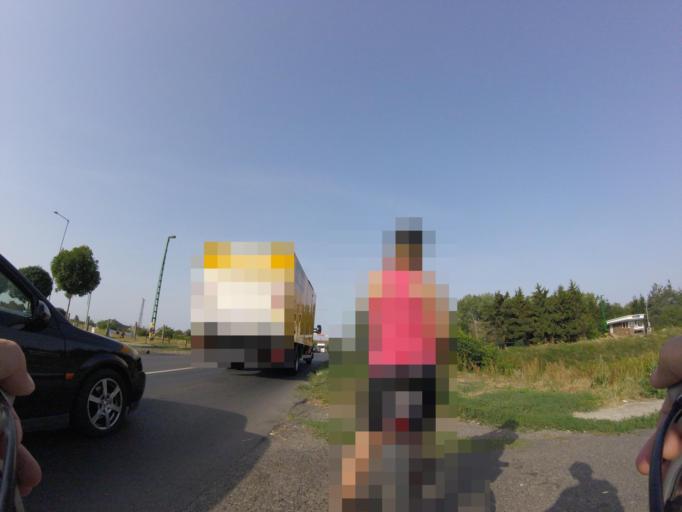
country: HU
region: Szabolcs-Szatmar-Bereg
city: Vasarosnameny
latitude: 48.1282
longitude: 22.3049
